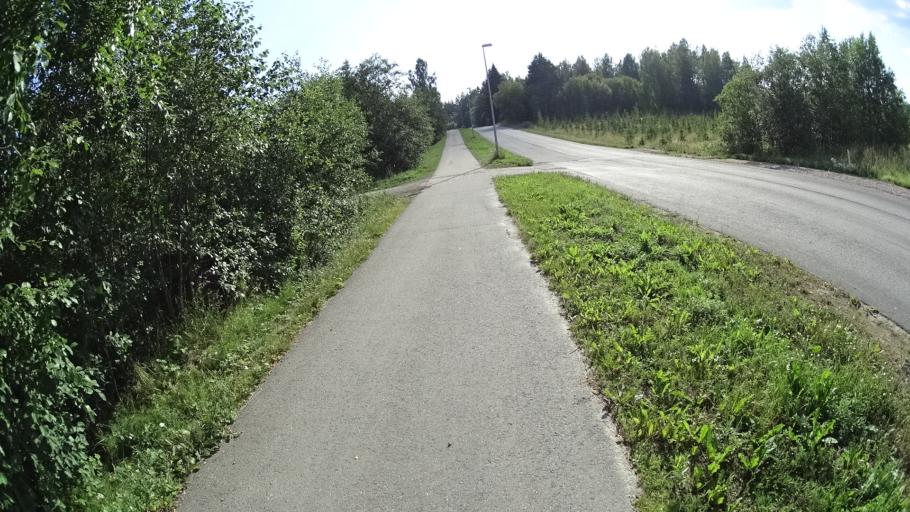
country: FI
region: Uusimaa
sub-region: Porvoo
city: Porvoo
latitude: 60.4132
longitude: 25.6535
